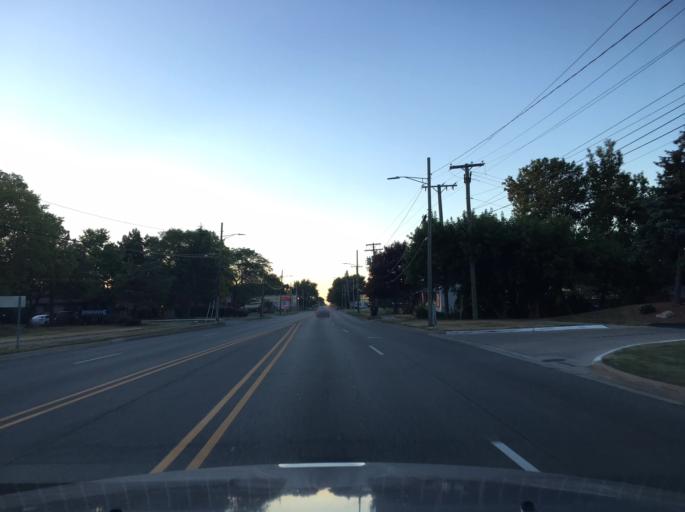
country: US
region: Michigan
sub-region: Macomb County
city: Roseville
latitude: 42.5176
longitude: -82.9405
